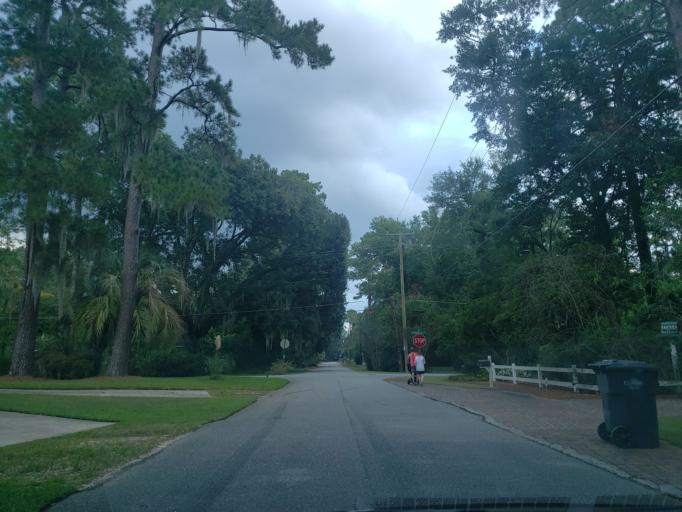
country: US
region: Georgia
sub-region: Chatham County
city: Isle of Hope
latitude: 31.9920
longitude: -81.0631
